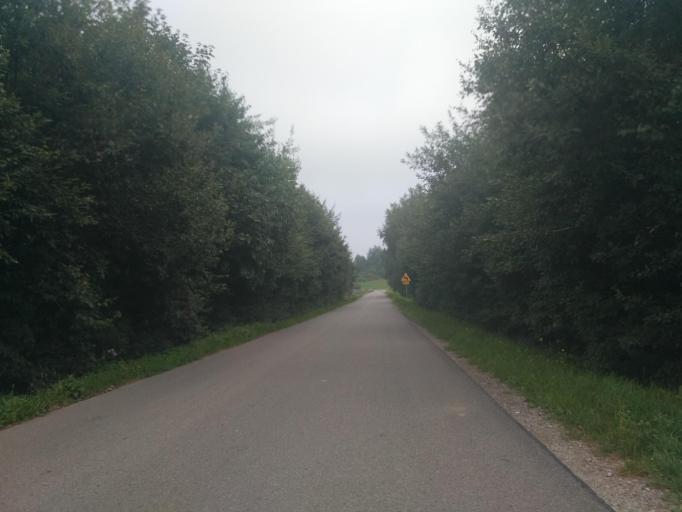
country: PL
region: Subcarpathian Voivodeship
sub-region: Powiat rzeszowski
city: Chmielnik
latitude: 50.0069
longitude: 22.1238
